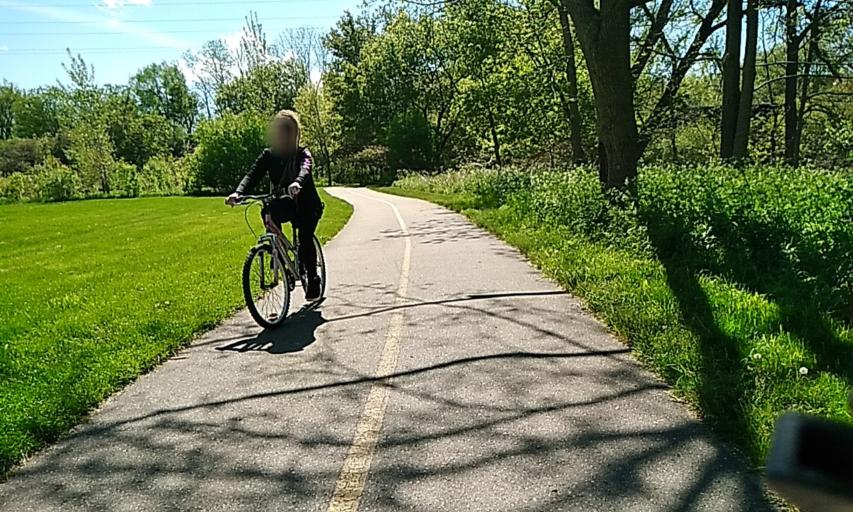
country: CA
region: Ontario
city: London
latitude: 42.9746
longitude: -81.2283
